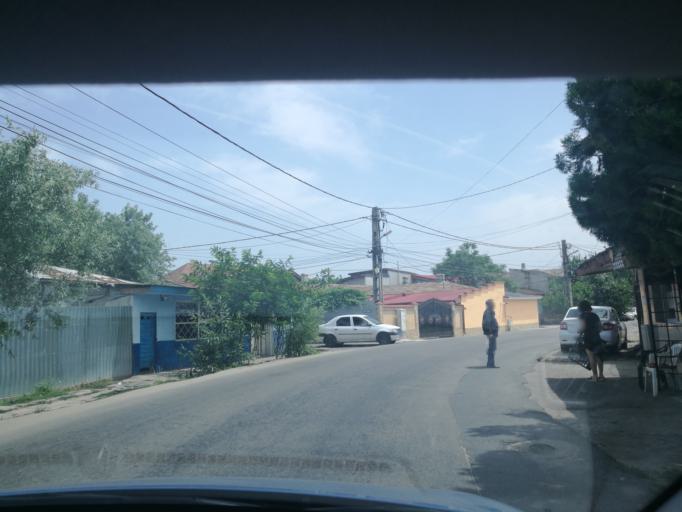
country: RO
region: Ilfov
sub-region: Comuna Jilava
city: Jilava
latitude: 44.3269
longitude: 26.0901
